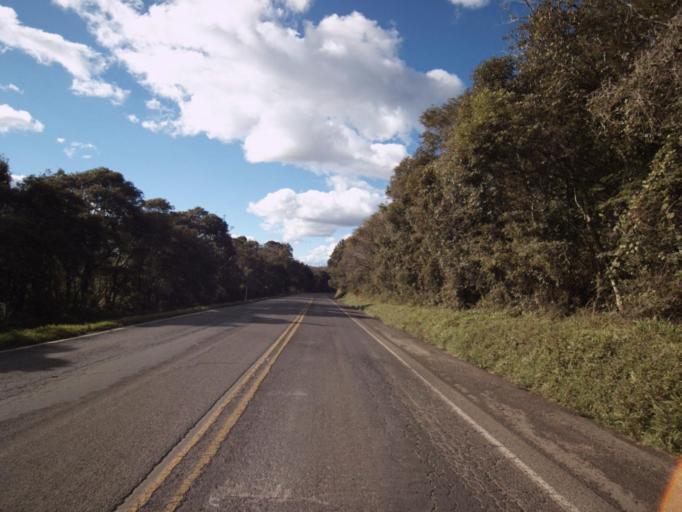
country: BR
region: Santa Catarina
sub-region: Joacaba
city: Joacaba
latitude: -27.1782
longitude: -51.5307
